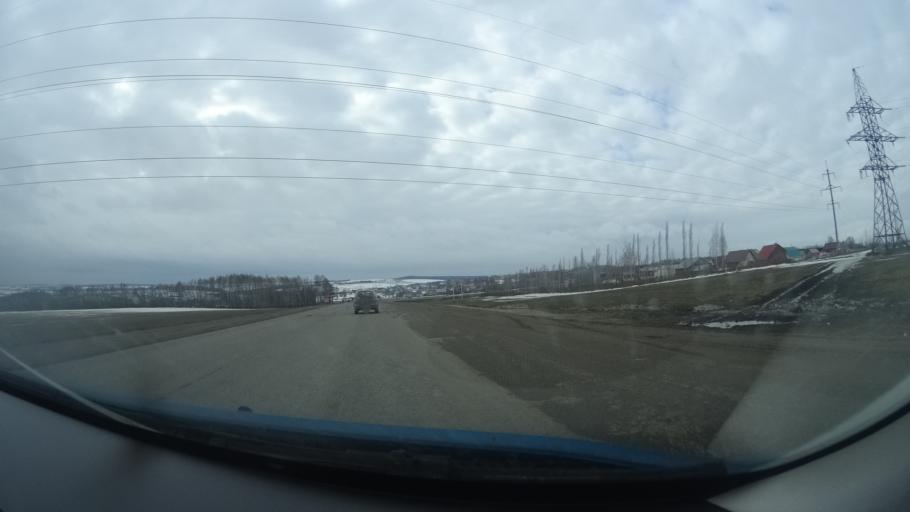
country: RU
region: Bashkortostan
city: Birsk
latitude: 55.4230
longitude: 55.5838
